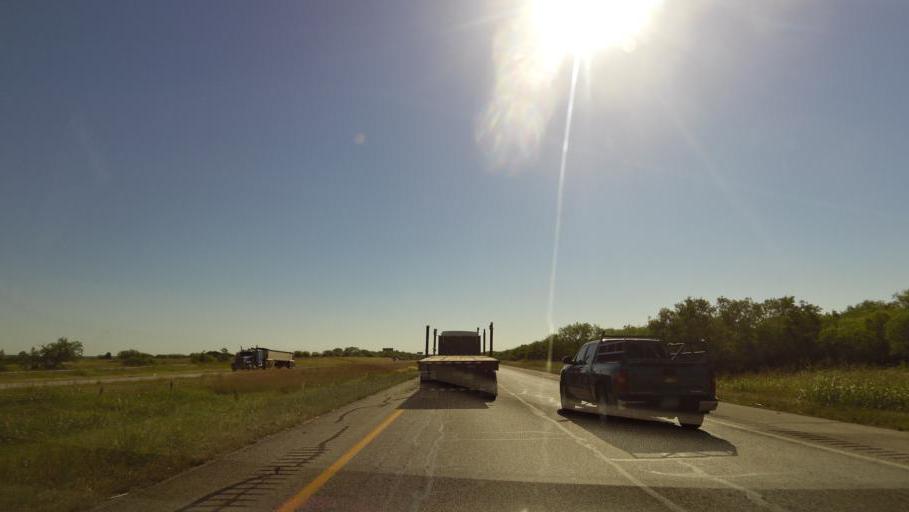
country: US
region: Texas
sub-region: Guadalupe County
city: Seguin
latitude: 29.6028
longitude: -97.9014
